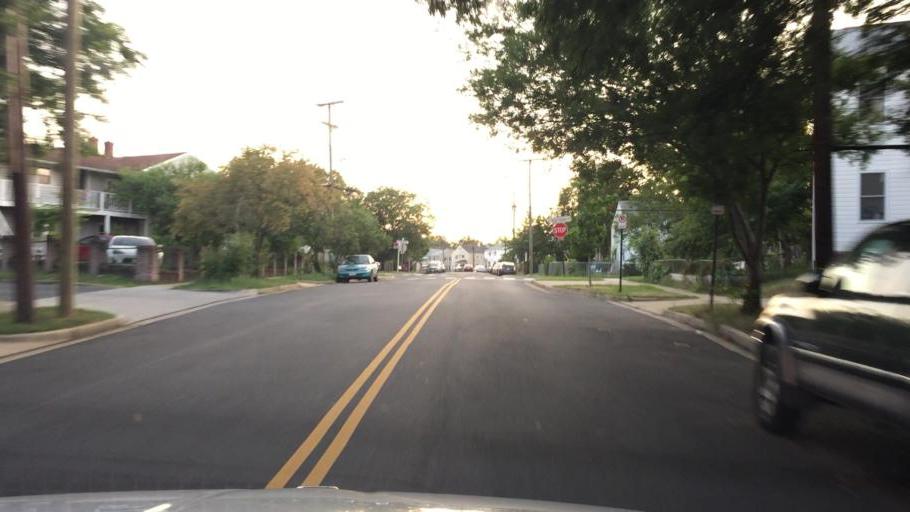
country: US
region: Virginia
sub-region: Fairfax County
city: Baileys Crossroads
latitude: 38.8565
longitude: -77.1203
